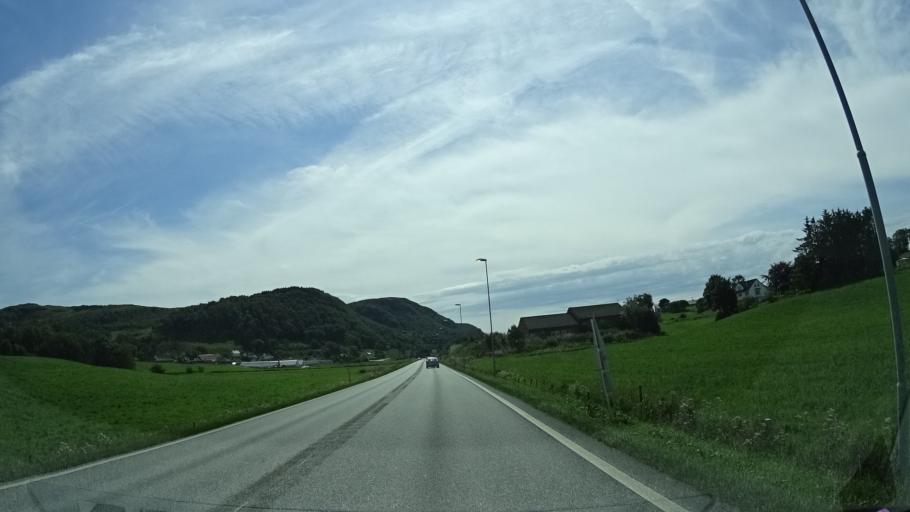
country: NO
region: Rogaland
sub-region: Rennesoy
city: Vikevag
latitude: 59.1125
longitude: 5.6983
